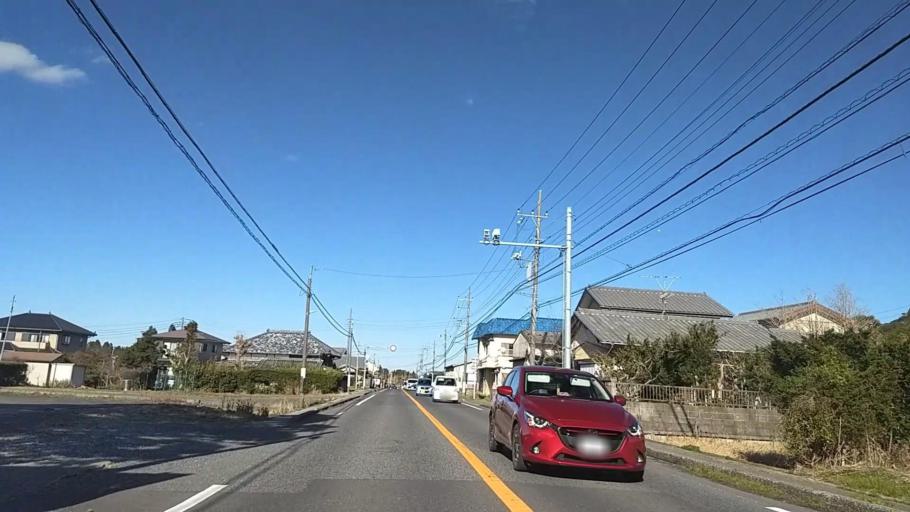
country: JP
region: Chiba
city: Ohara
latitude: 35.2306
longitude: 140.3878
